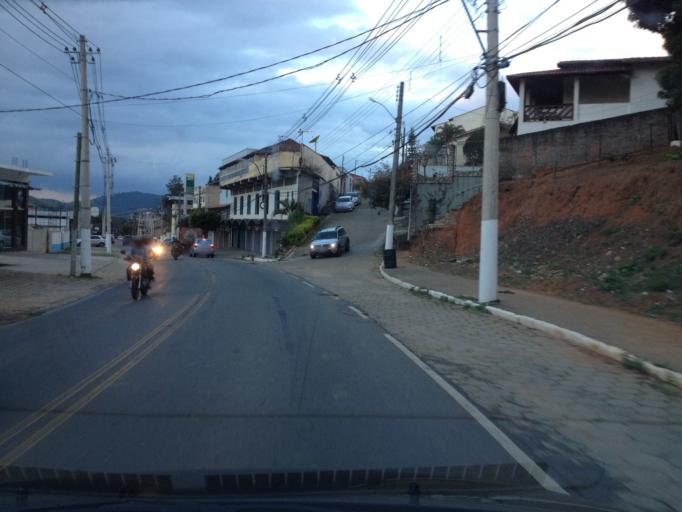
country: BR
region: Minas Gerais
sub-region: Sao Lourenco
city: Sao Lourenco
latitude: -22.1046
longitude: -45.0532
